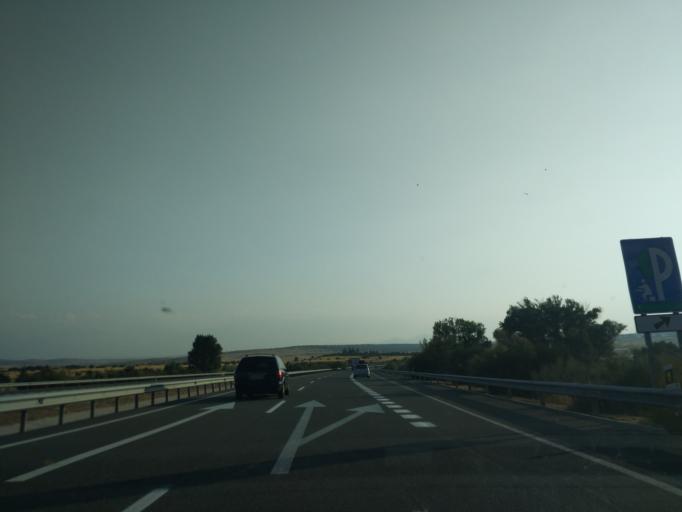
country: ES
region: Castille and Leon
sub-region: Provincia de Avila
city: Berrocalejo de Aragona
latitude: 40.6934
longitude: -4.5844
